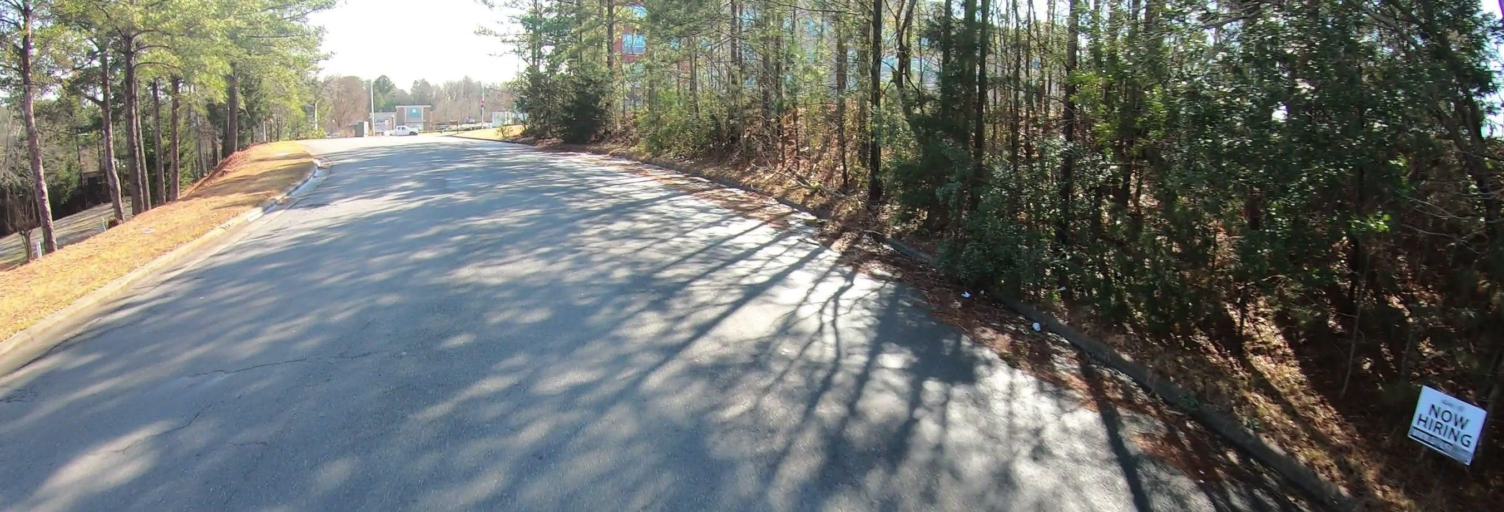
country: US
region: South Carolina
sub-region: York County
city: Fort Mill
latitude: 35.0328
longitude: -80.9667
